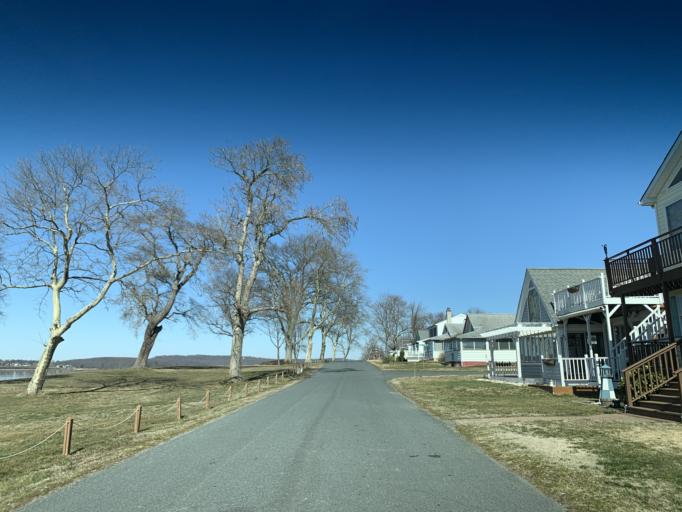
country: US
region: Maryland
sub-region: Cecil County
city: Charlestown
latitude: 39.4391
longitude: -75.9780
